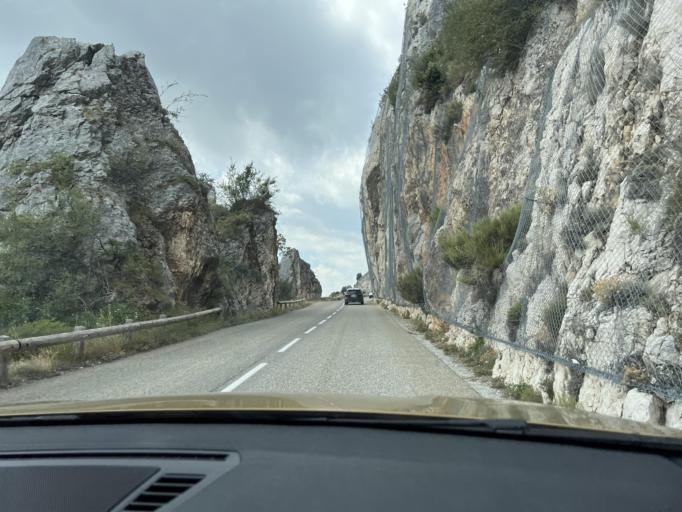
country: FR
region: Provence-Alpes-Cote d'Azur
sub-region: Departement des Alpes-Maritimes
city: Saint-Vallier-de-Thiey
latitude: 43.7970
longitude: 6.9251
